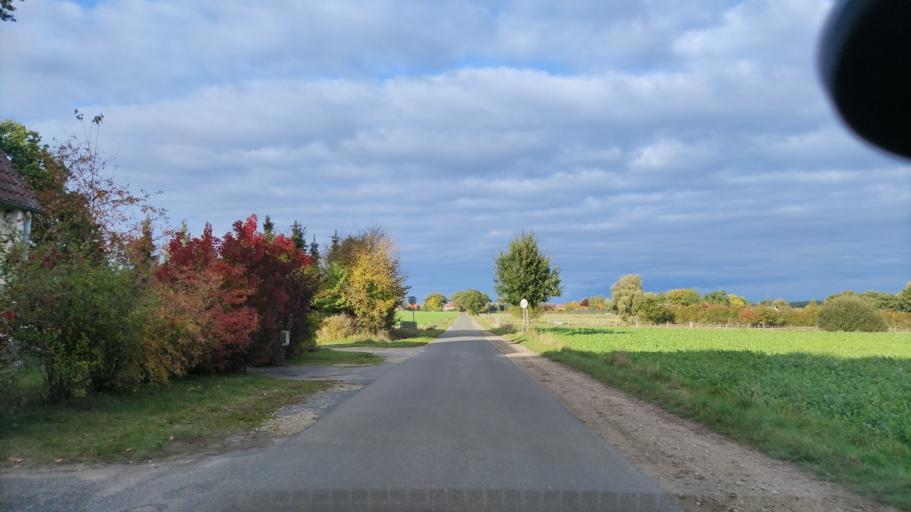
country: DE
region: Lower Saxony
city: Jelmstorf
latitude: 53.1374
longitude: 10.5302
